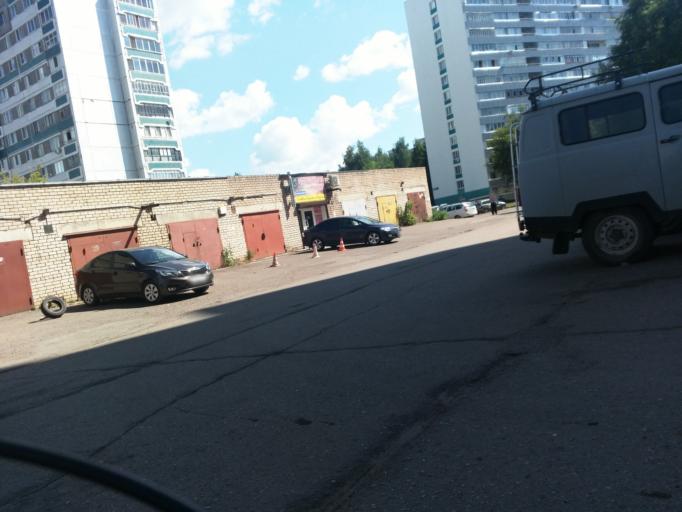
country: RU
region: Tatarstan
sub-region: Tukayevskiy Rayon
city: Naberezhnyye Chelny
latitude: 55.7458
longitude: 52.4033
